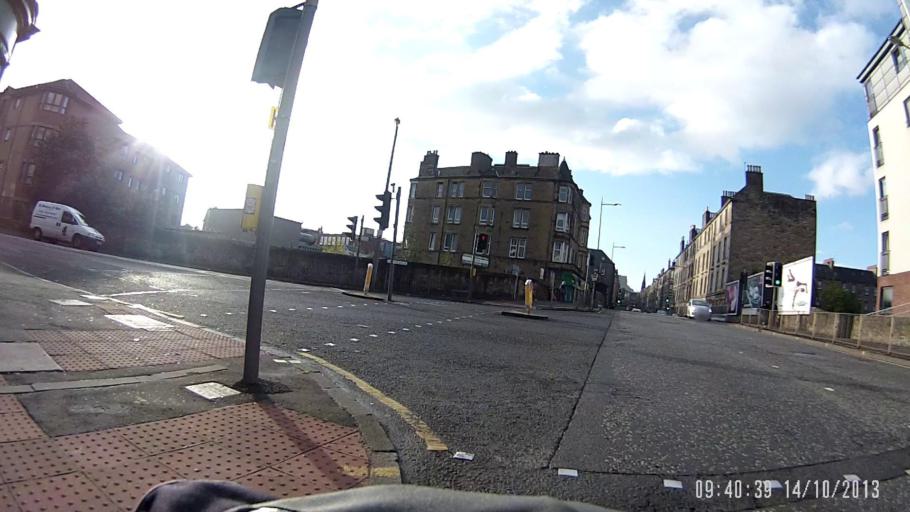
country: GB
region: Scotland
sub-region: West Lothian
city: Seafield
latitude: 55.9617
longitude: -3.1711
